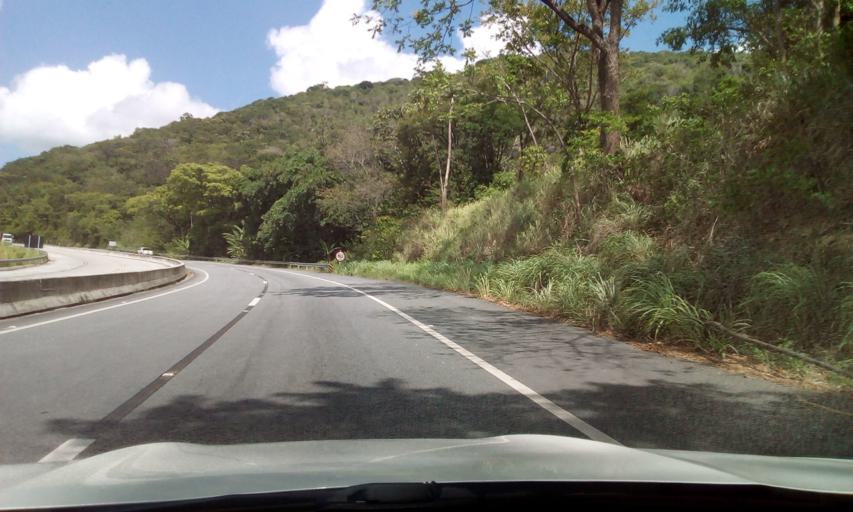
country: BR
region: Alagoas
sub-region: Flexeiras
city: Flexeiras
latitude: -9.2488
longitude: -35.7626
